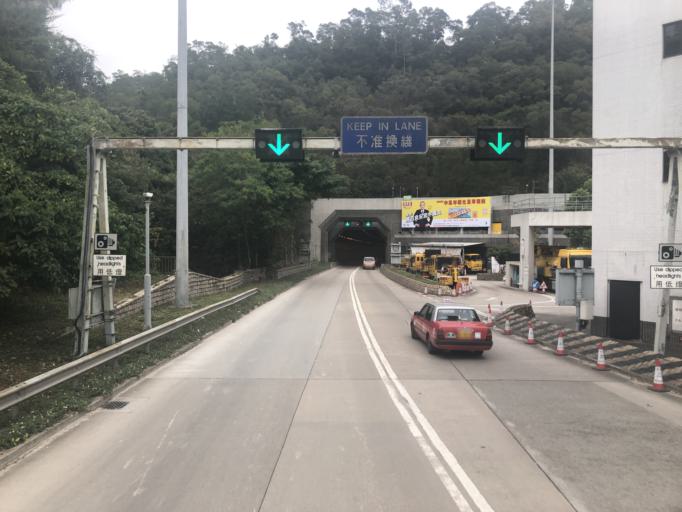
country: HK
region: Kowloon City
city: Kowloon
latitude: 22.3169
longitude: 114.2417
